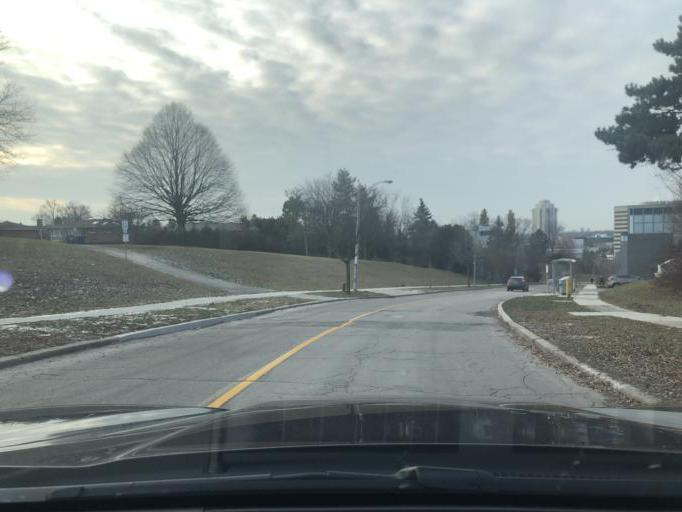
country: CA
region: Ontario
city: Willowdale
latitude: 43.7636
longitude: -79.3449
